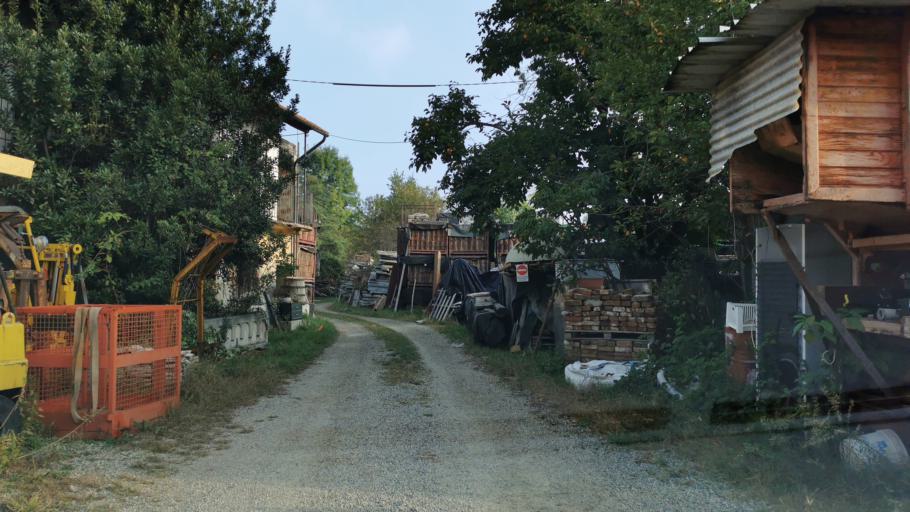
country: IT
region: Piedmont
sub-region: Provincia di Torino
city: Front
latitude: 45.2560
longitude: 7.6683
